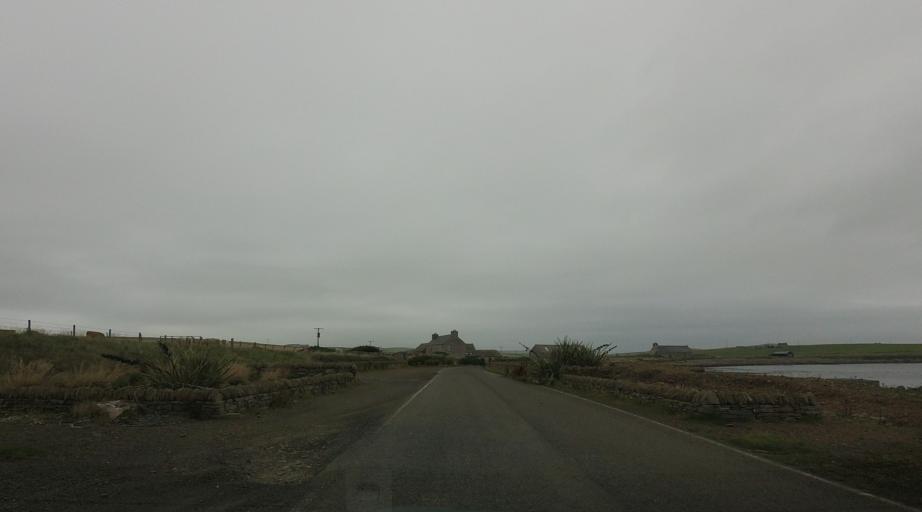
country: GB
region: Scotland
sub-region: Orkney Islands
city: Orkney
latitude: 58.7406
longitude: -2.9725
